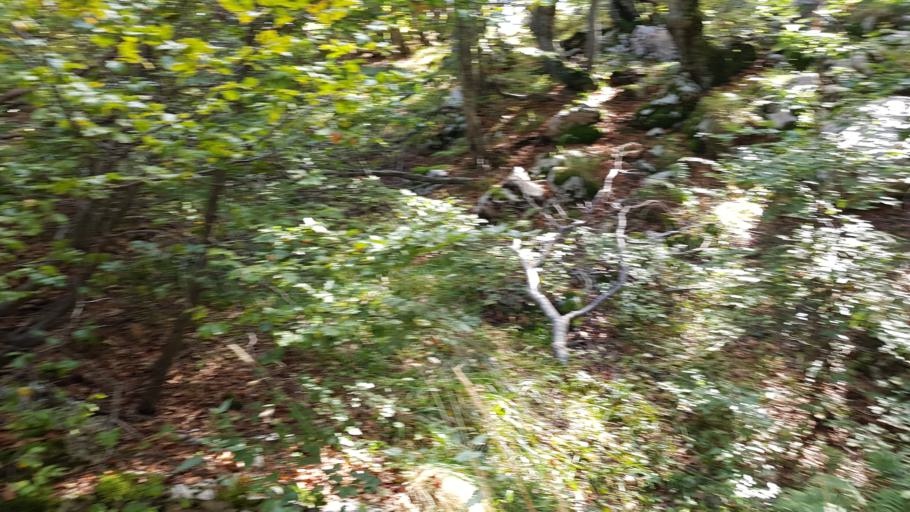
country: SI
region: Kobarid
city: Kobarid
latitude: 46.2906
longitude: 13.6090
